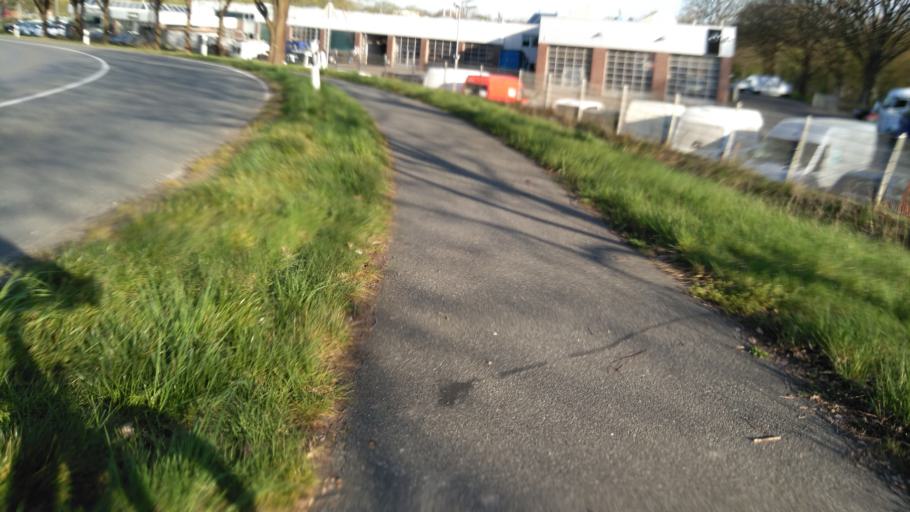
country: DE
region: Lower Saxony
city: Buxtehude
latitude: 53.4615
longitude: 9.6984
